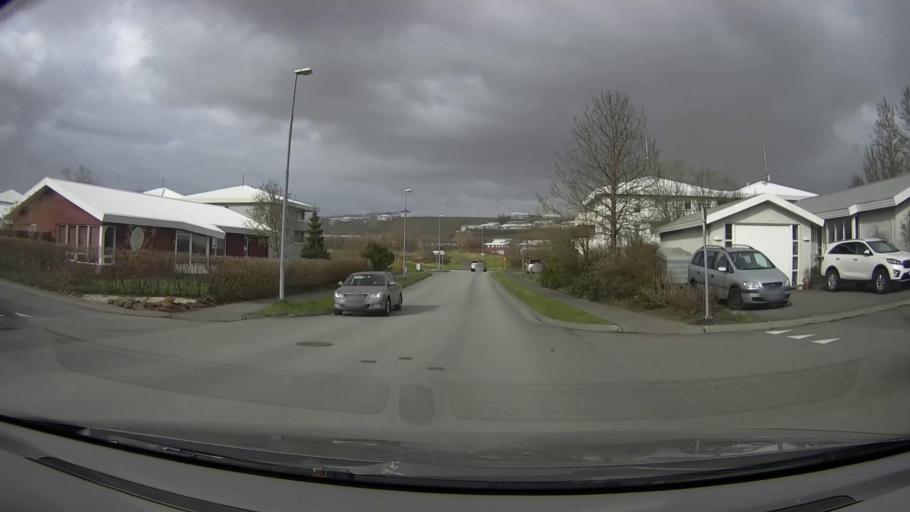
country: IS
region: Capital Region
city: Hafnarfjoerdur
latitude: 64.0588
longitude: -21.9303
